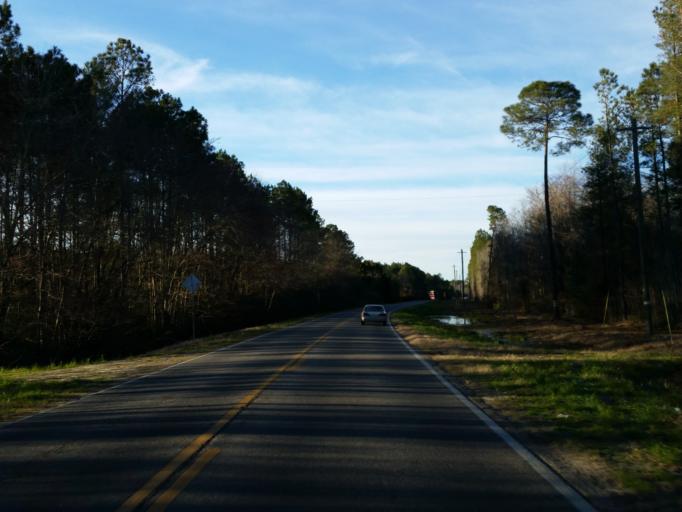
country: US
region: Georgia
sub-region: Cook County
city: Sparks
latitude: 31.2092
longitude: -83.4518
